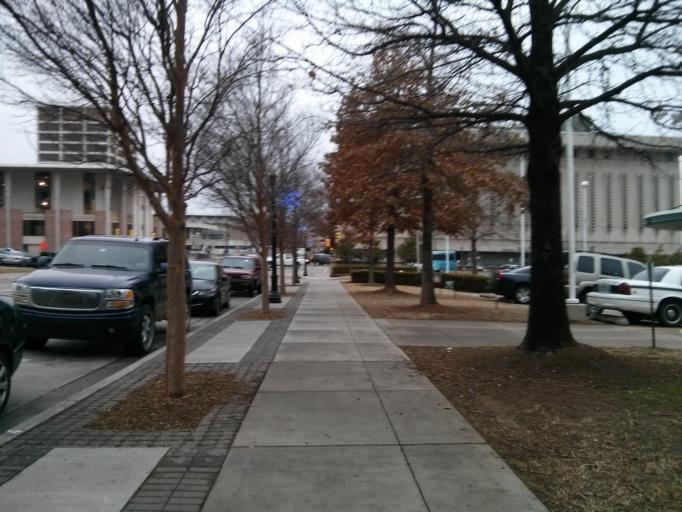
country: US
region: Oklahoma
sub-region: Tulsa County
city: Tulsa
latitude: 36.1516
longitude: -95.9934
